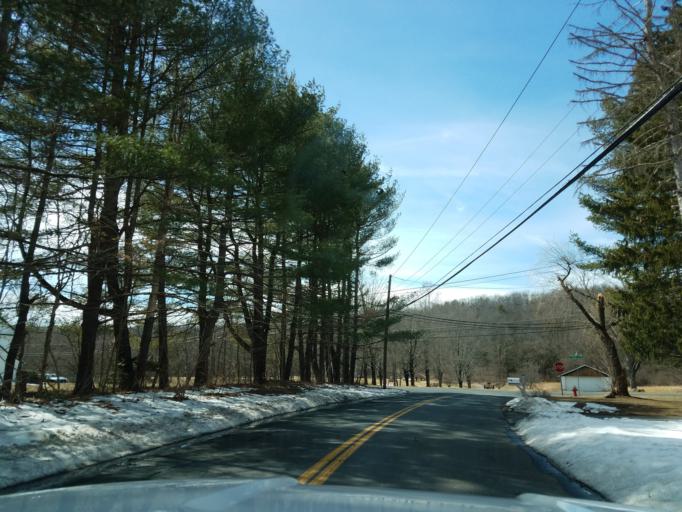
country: US
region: Connecticut
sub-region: Hartford County
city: Canton Valley
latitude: 41.8033
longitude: -72.8877
